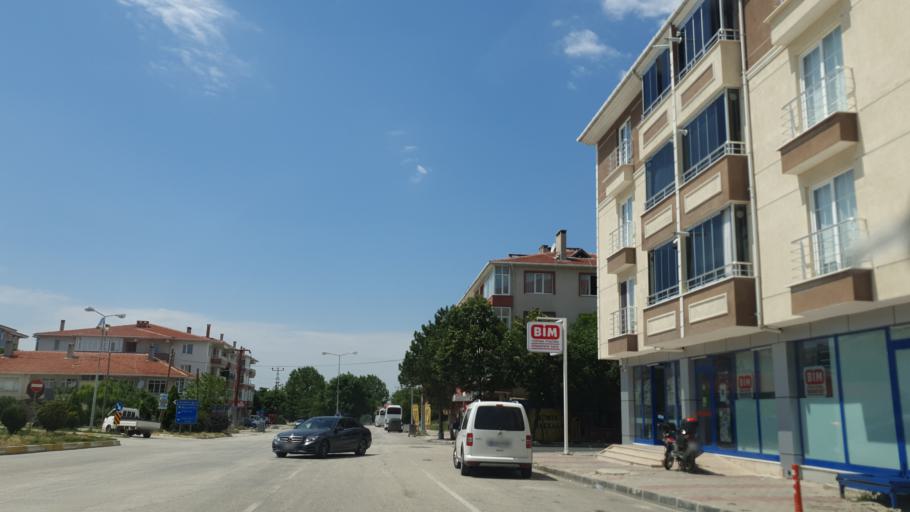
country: TR
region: Tekirdag
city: Saray
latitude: 41.4407
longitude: 27.9137
